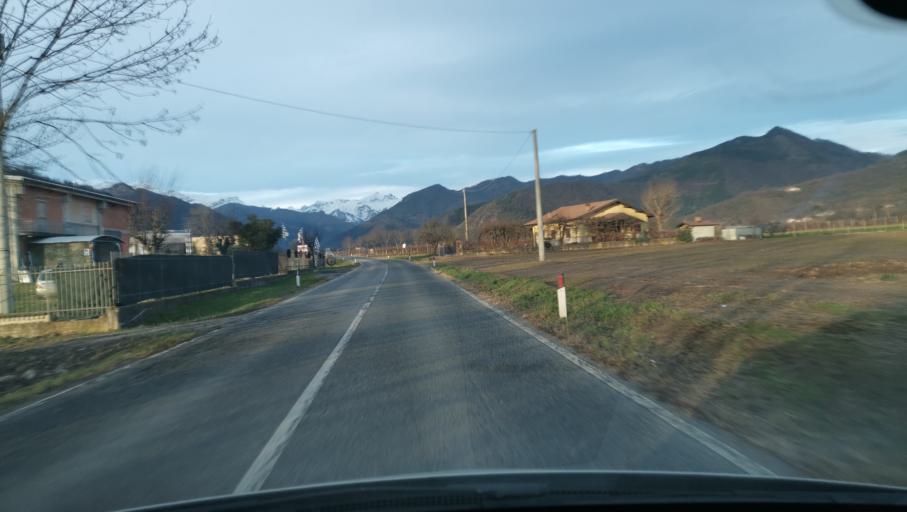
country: IT
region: Piedmont
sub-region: Provincia di Cuneo
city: Valgrana
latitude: 44.4138
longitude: 7.4003
